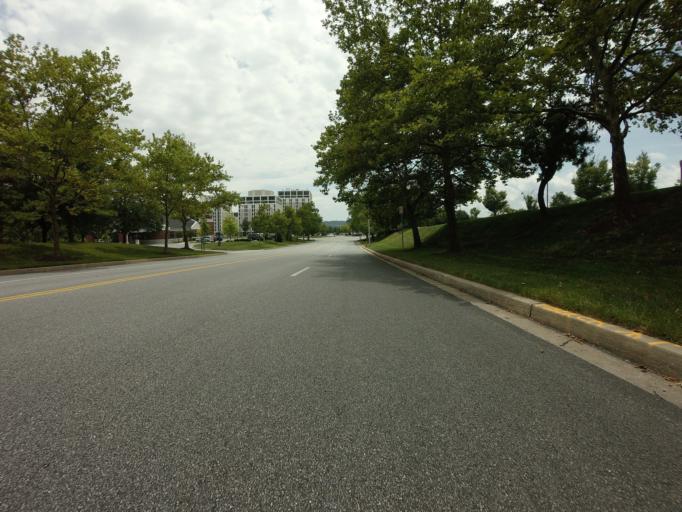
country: US
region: Maryland
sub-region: Baltimore County
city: Hunt Valley
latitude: 39.4965
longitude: -76.6617
